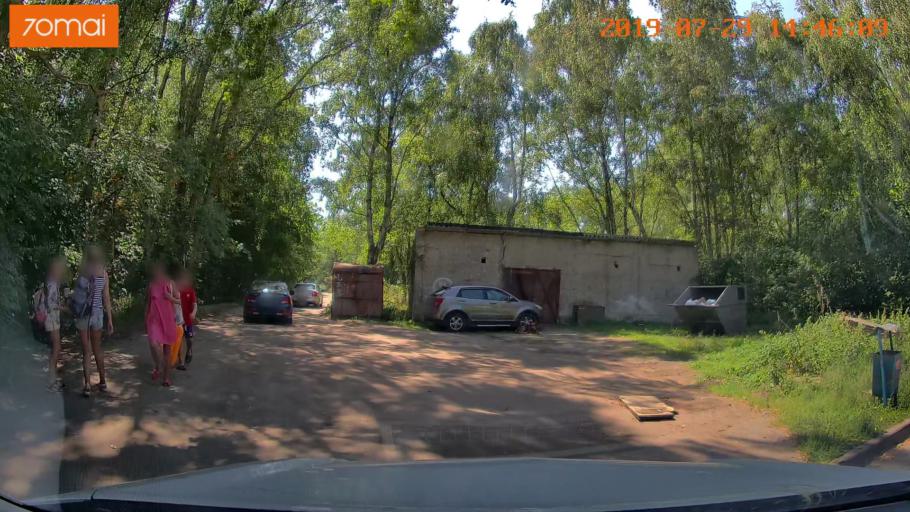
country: RU
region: Kaliningrad
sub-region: Gorod Kaliningrad
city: Baltiysk
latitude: 54.6644
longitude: 19.9027
